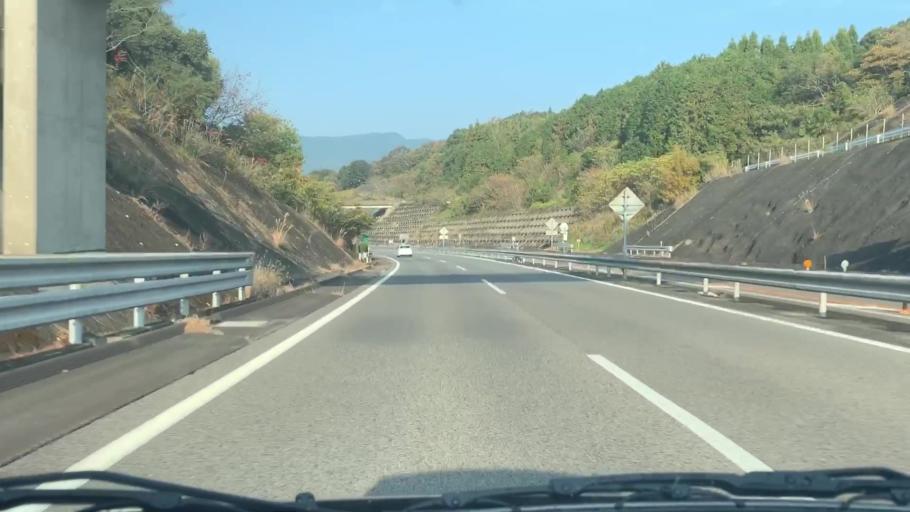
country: JP
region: Saga Prefecture
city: Imaricho-ko
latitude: 33.1678
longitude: 129.8555
